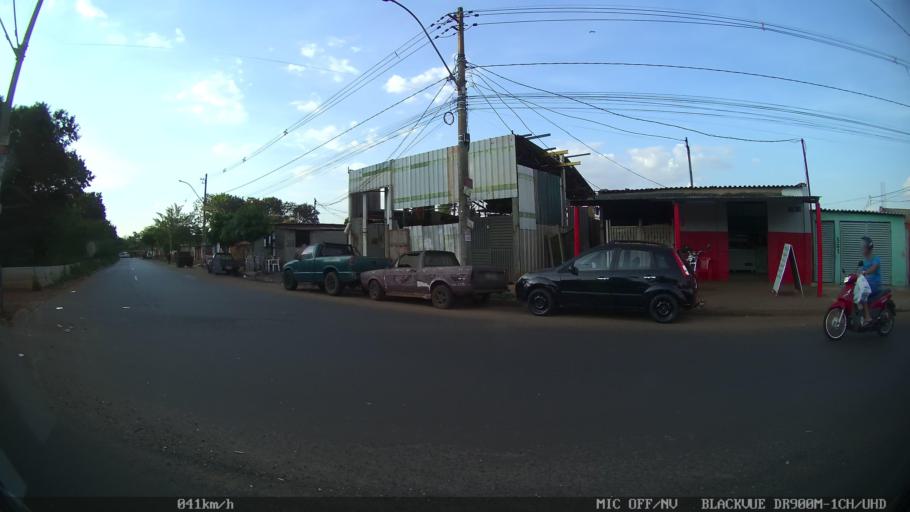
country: BR
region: Sao Paulo
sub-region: Ribeirao Preto
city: Ribeirao Preto
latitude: -21.1183
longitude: -47.8030
